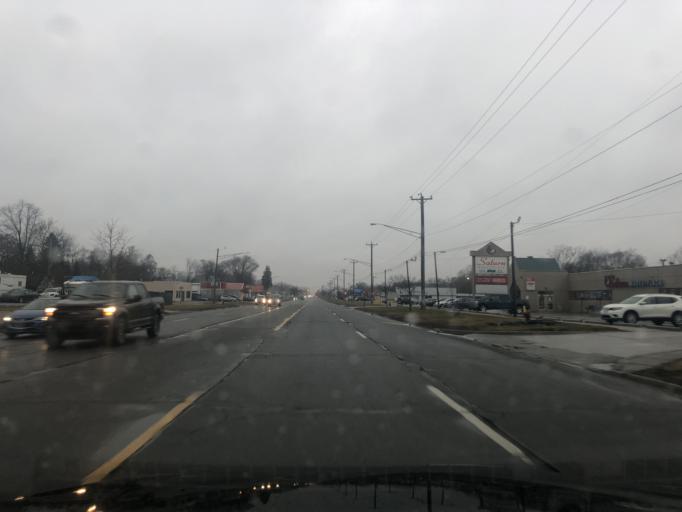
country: US
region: Michigan
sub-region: Wayne County
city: Taylor
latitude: 42.2689
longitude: -83.2809
